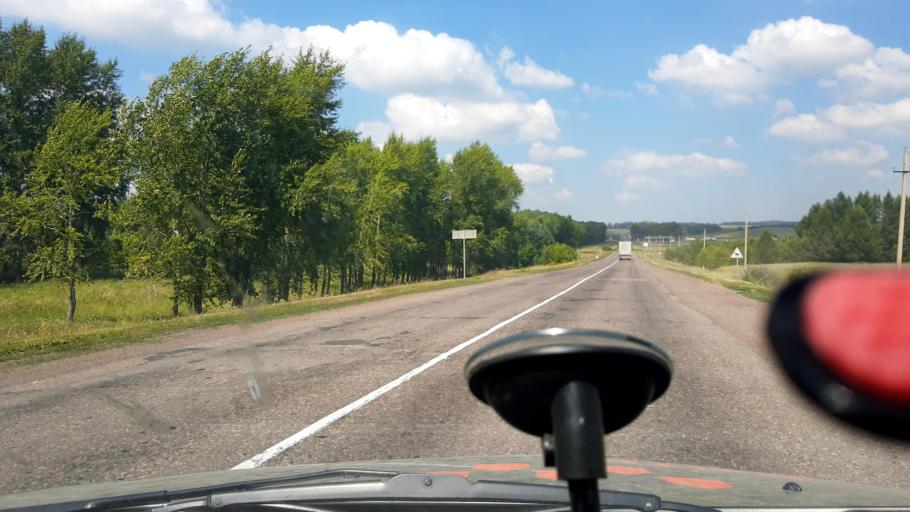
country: RU
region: Bashkortostan
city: Chekmagush
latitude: 54.8895
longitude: 54.5782
